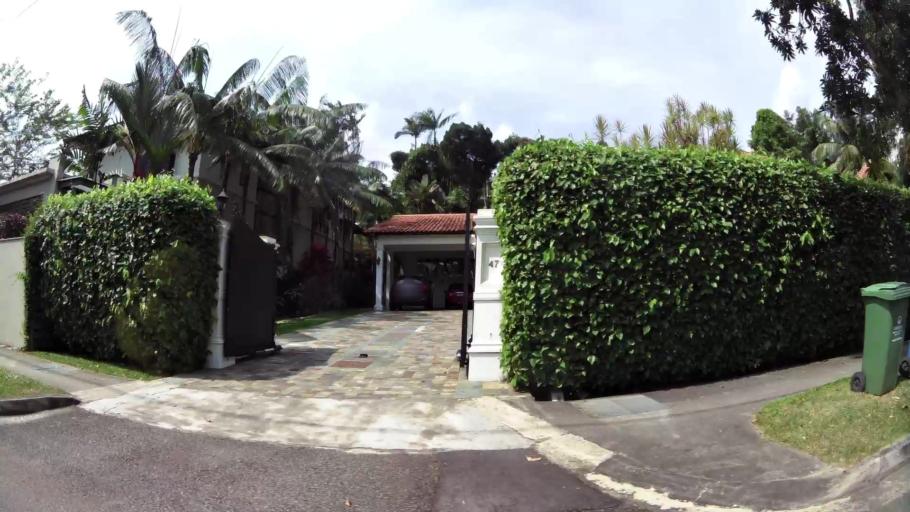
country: SG
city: Singapore
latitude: 1.3398
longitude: 103.7875
